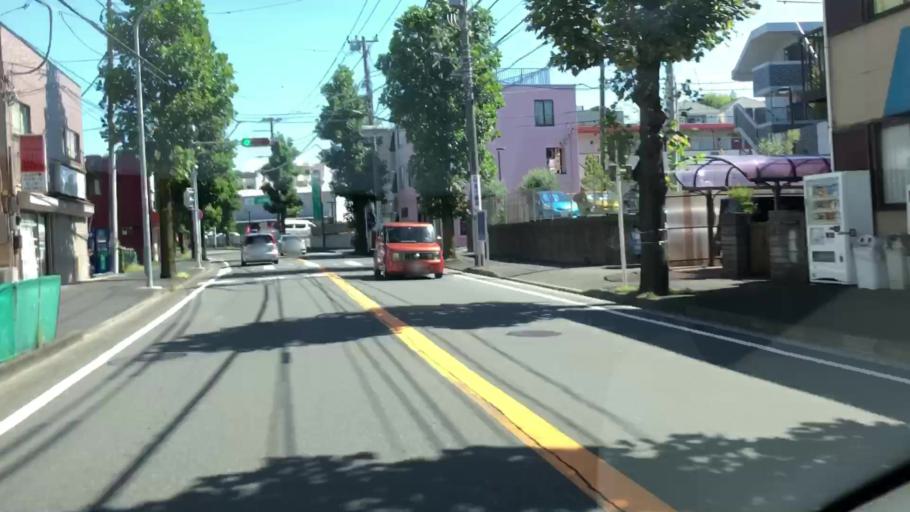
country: JP
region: Kanagawa
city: Yokohama
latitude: 35.3854
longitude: 139.6023
